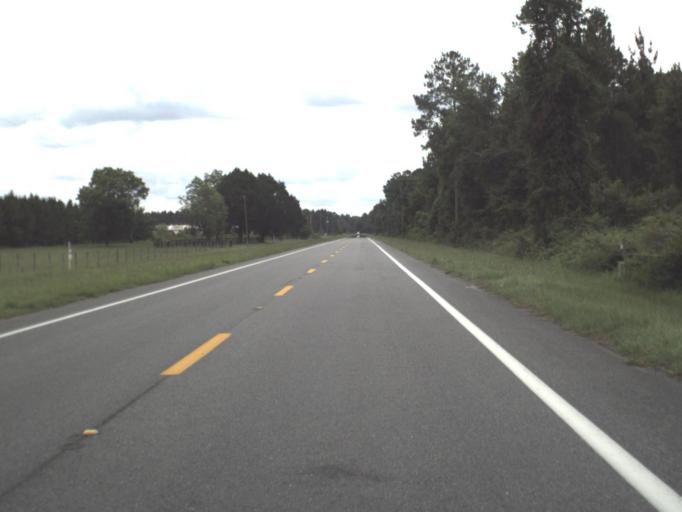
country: US
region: Florida
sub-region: Union County
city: Lake Butler
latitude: 30.0332
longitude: -82.3692
